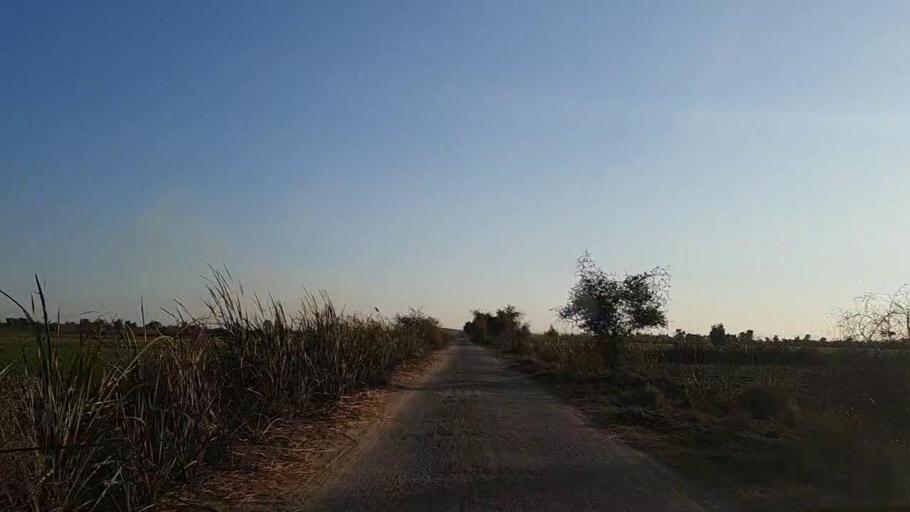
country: PK
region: Sindh
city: Khadro
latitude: 26.2702
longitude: 68.8099
